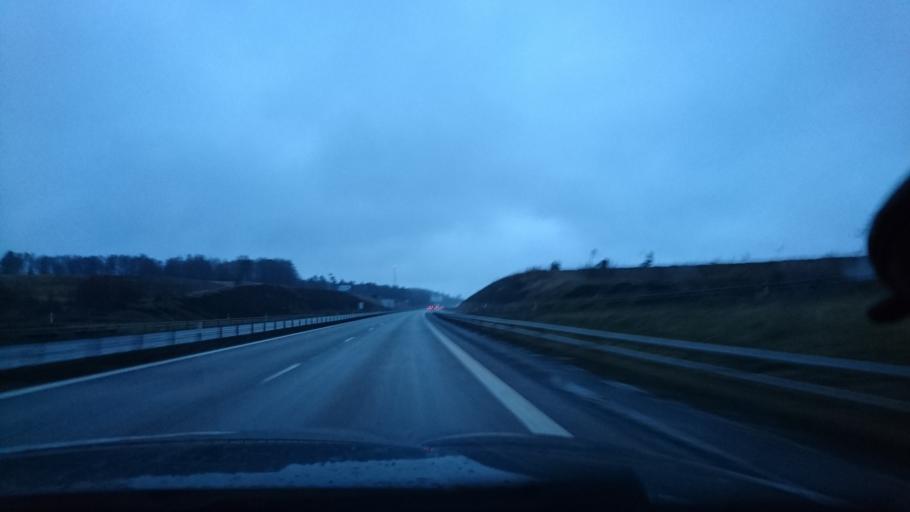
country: SE
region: Skane
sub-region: Orkelljunga Kommun
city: OErkelljunga
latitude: 56.2851
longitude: 13.3430
